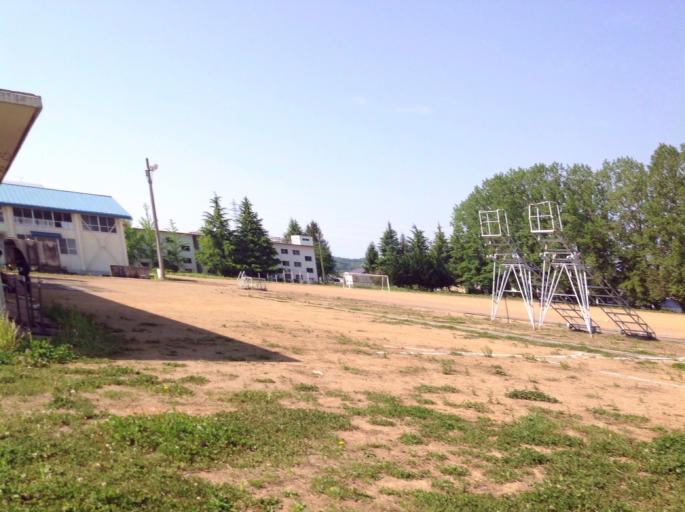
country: JP
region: Iwate
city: Ichinoseki
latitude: 38.9249
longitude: 141.1063
